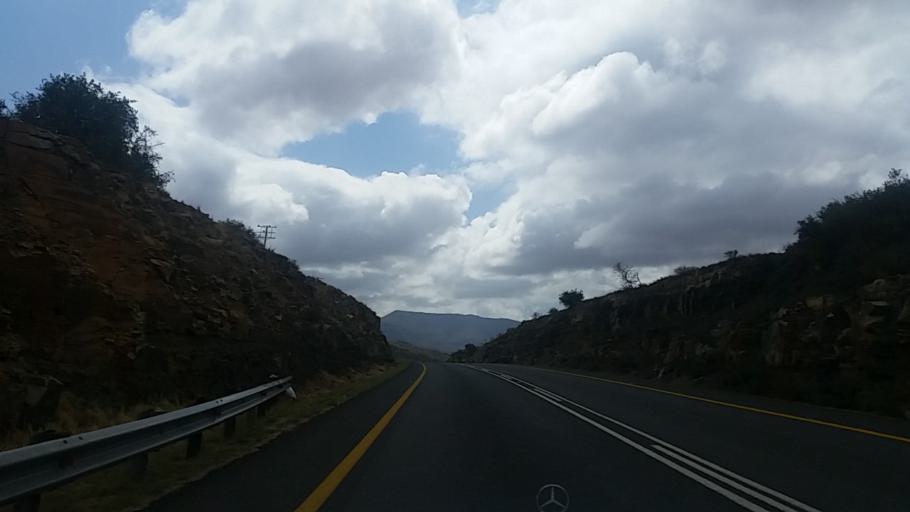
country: ZA
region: Eastern Cape
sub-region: Cacadu District Municipality
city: Graaff-Reinet
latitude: -32.1093
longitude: 24.6087
